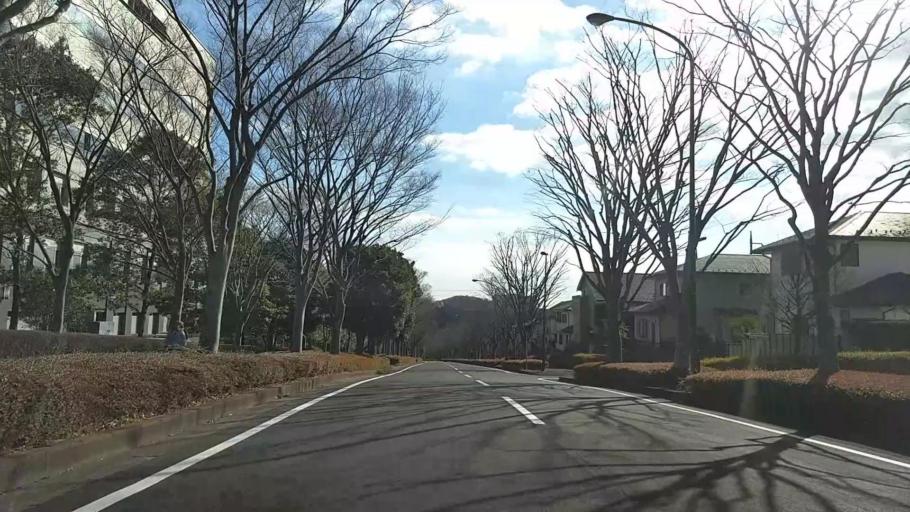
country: JP
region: Kanagawa
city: Atsugi
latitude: 35.4526
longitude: 139.3057
